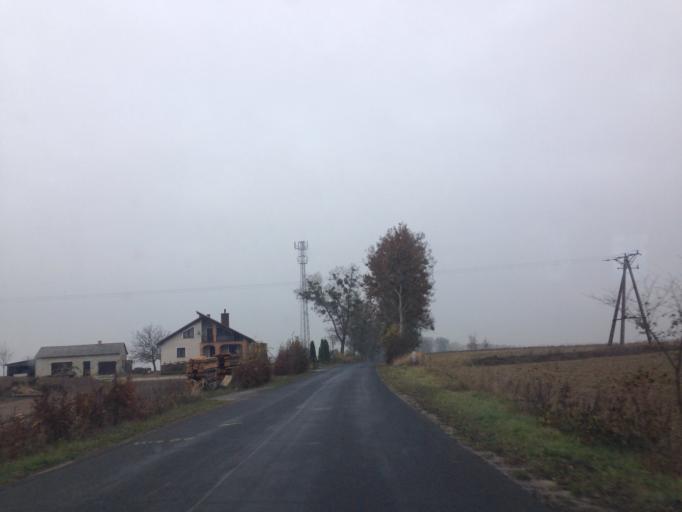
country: PL
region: Kujawsko-Pomorskie
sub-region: Powiat brodnicki
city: Gorzno
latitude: 53.2034
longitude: 19.6371
